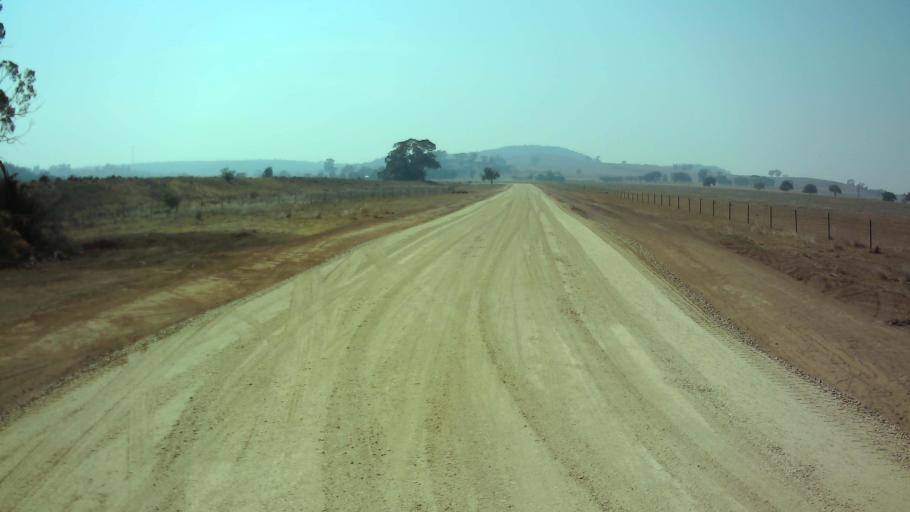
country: AU
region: New South Wales
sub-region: Weddin
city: Grenfell
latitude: -33.8559
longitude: 148.1078
